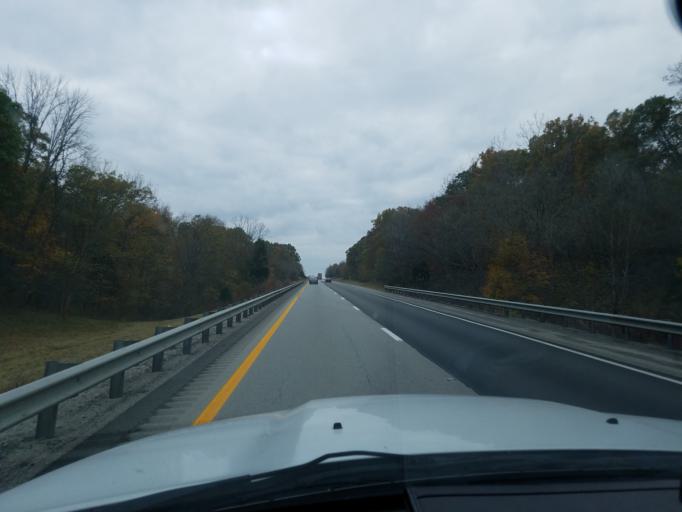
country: US
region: Kentucky
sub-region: Oldham County
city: La Grange
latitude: 38.4168
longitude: -85.3408
